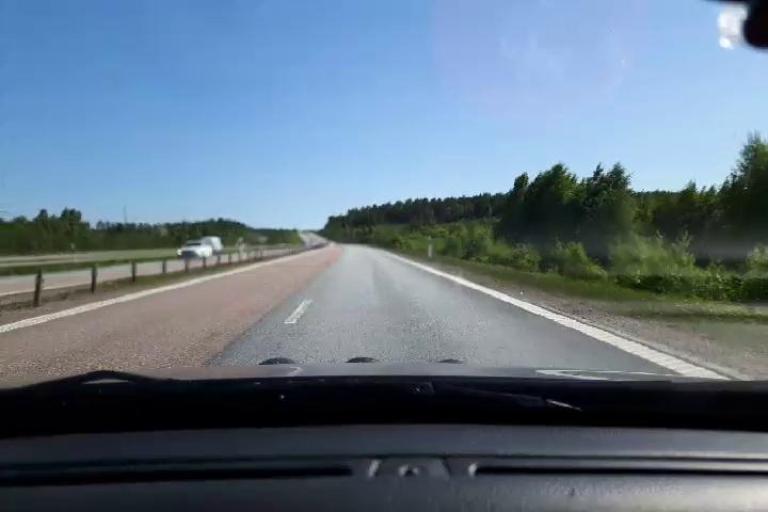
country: SE
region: Gaevleborg
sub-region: Soderhamns Kommun
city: Soderhamn
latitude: 61.3558
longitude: 17.0154
